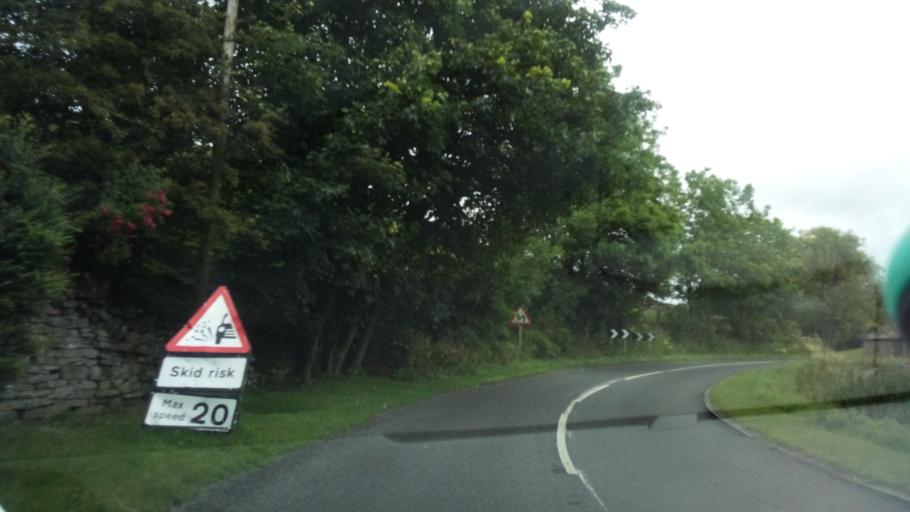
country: GB
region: England
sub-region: County Durham
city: Mickleton
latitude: 54.6099
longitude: -2.0827
